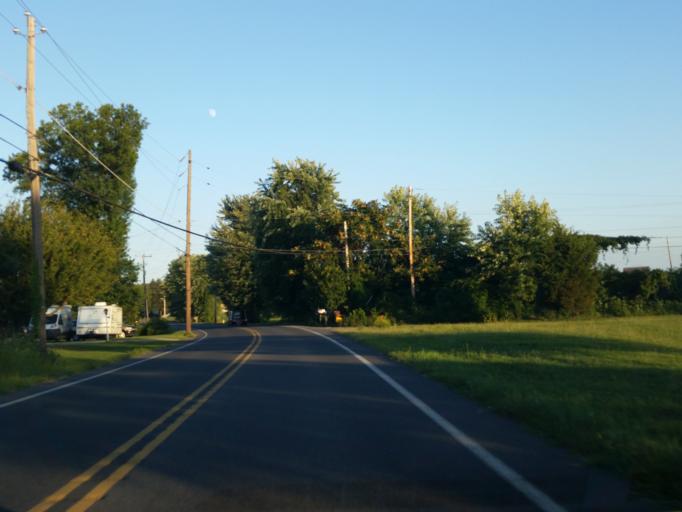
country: US
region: Pennsylvania
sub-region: Lebanon County
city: Sand Hill
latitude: 40.3762
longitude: -76.4407
